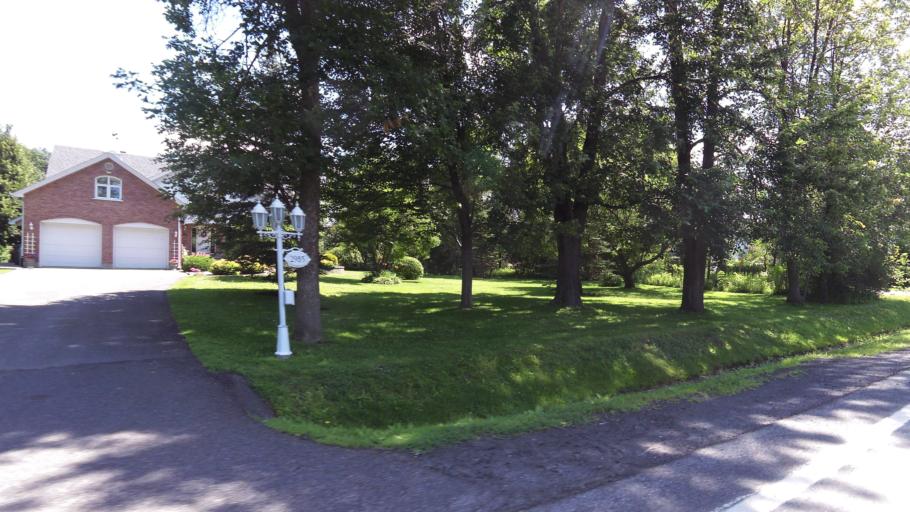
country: CA
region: Quebec
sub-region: Monteregie
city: Richelieu
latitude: 45.4362
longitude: -73.2547
